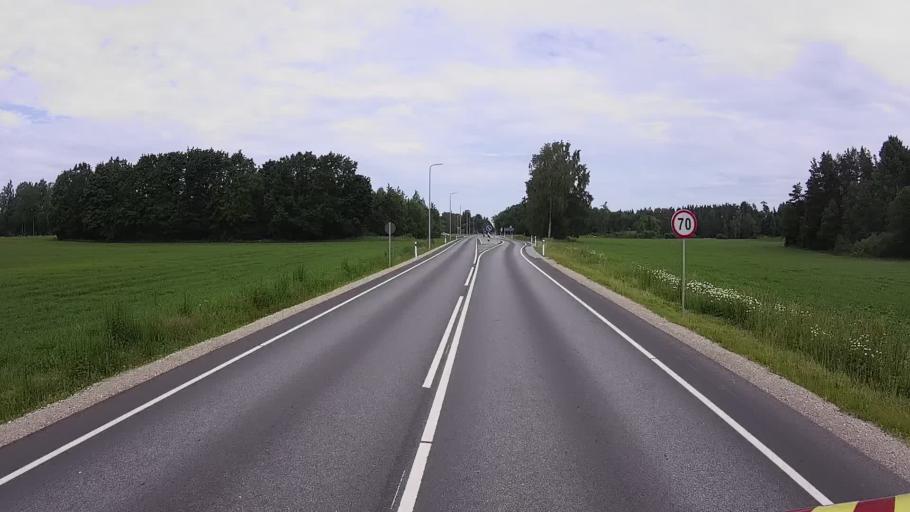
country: EE
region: Viljandimaa
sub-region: Viljandi linn
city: Viljandi
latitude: 58.2391
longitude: 25.5959
